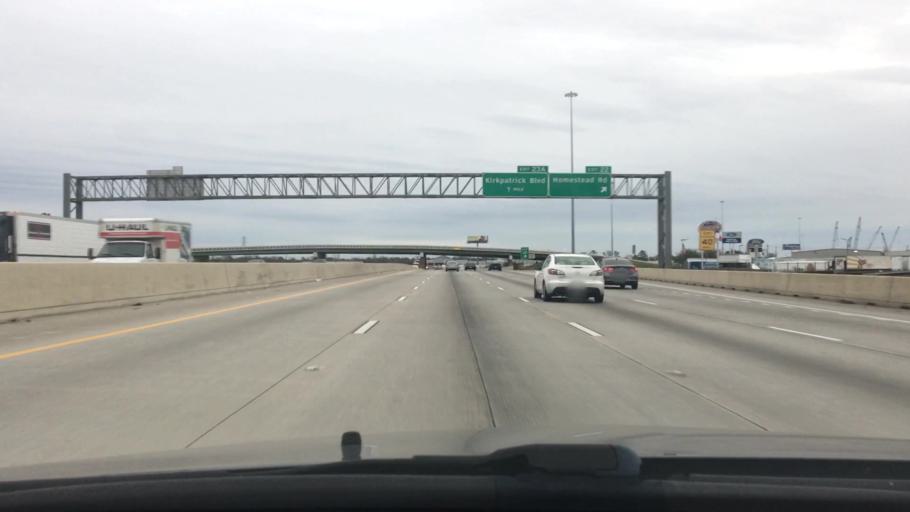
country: US
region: Texas
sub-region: Harris County
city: Houston
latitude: 29.8094
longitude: -95.3100
